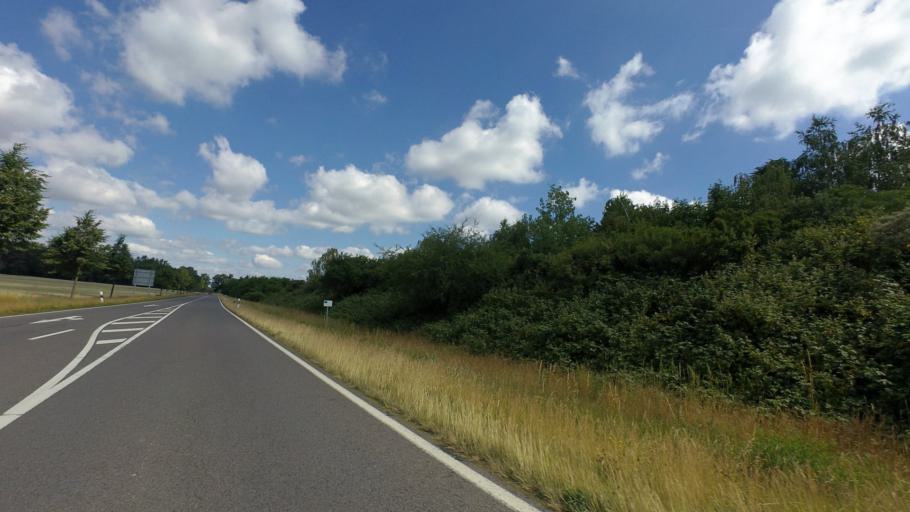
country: DE
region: Saxony
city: Kamenz
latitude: 51.3165
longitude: 14.0900
